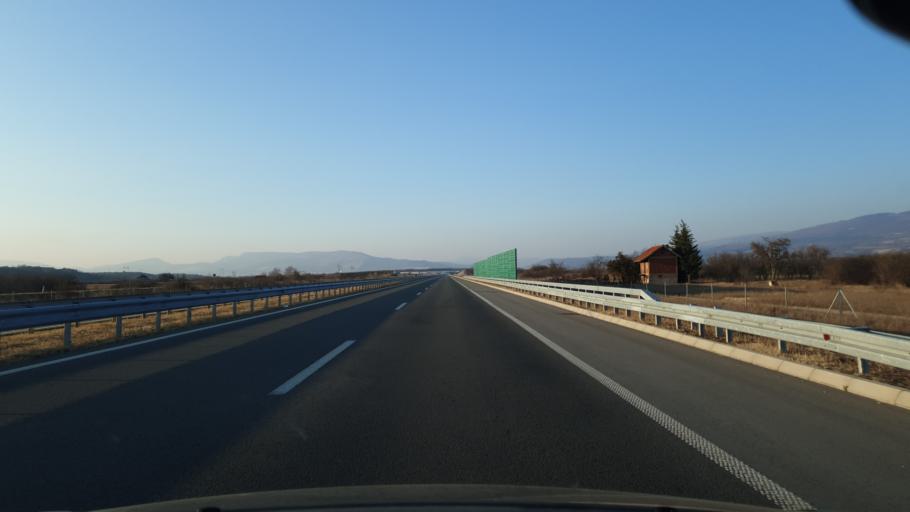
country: RS
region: Central Serbia
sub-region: Pirotski Okrug
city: Pirot
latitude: 43.1010
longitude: 22.6426
